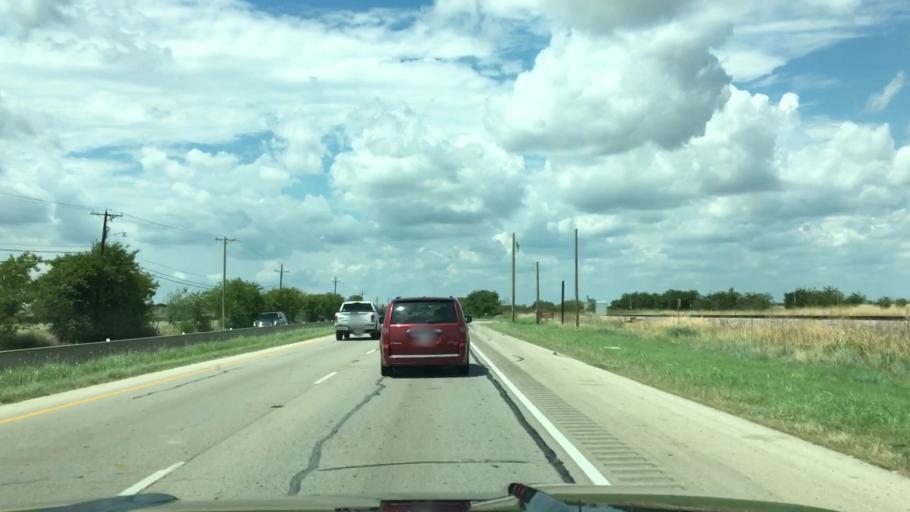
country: US
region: Texas
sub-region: Tarrant County
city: Saginaw
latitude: 32.8879
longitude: -97.3877
